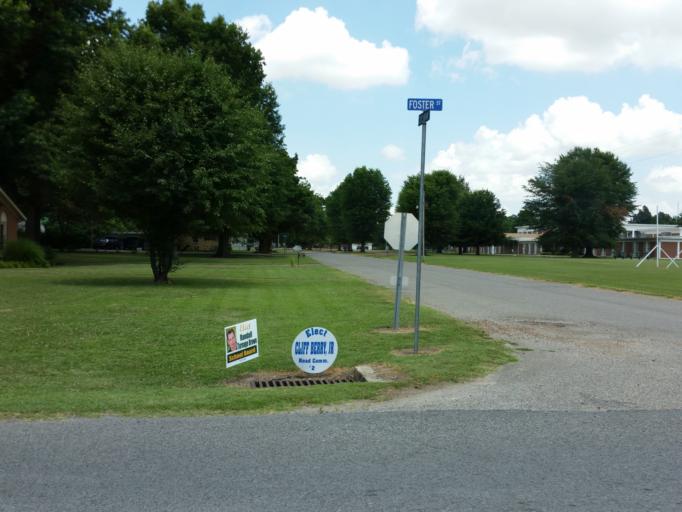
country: US
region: Tennessee
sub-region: Lake County
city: Tiptonville
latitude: 36.3737
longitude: -89.4737
